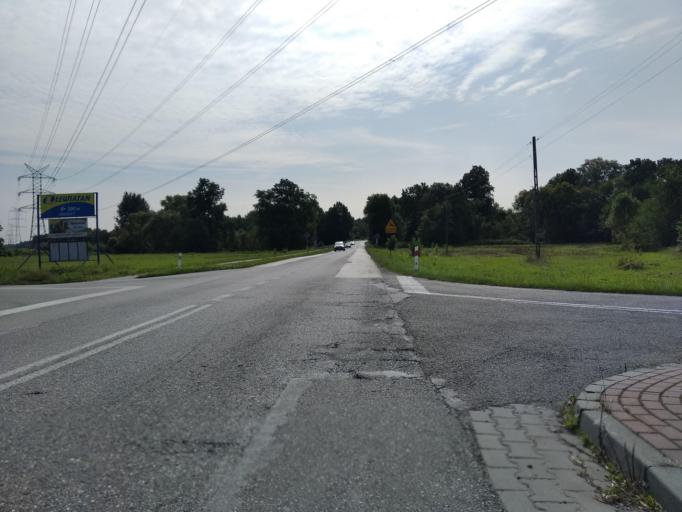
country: PL
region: Subcarpathian Voivodeship
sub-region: Powiat ropczycko-sedziszowski
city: Ostrow
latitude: 50.1403
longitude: 21.5851
